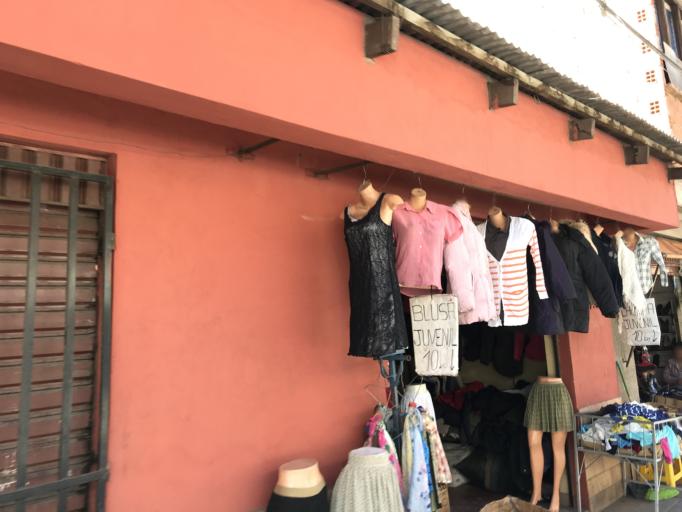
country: BO
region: Chuquisaca
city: Sucre
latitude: -19.0356
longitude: -65.2541
